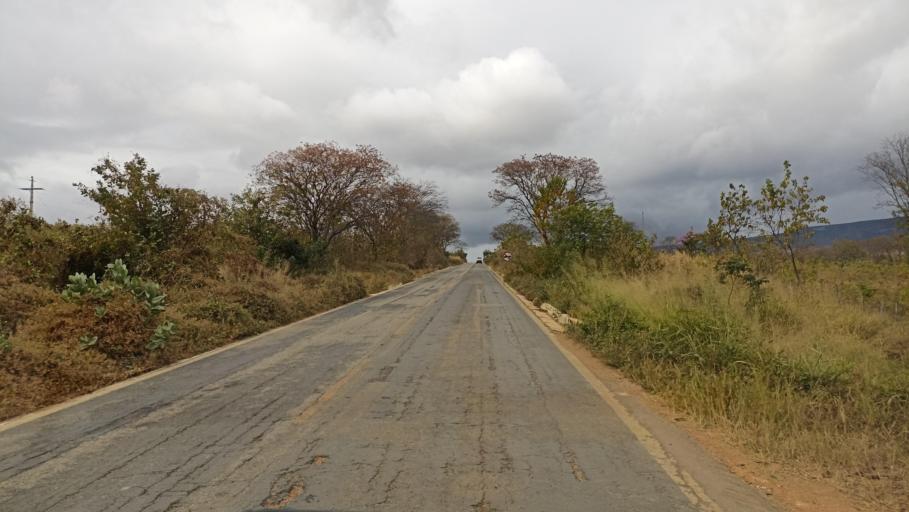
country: BR
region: Minas Gerais
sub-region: Itinga
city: Itinga
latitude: -16.6275
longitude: -41.7870
